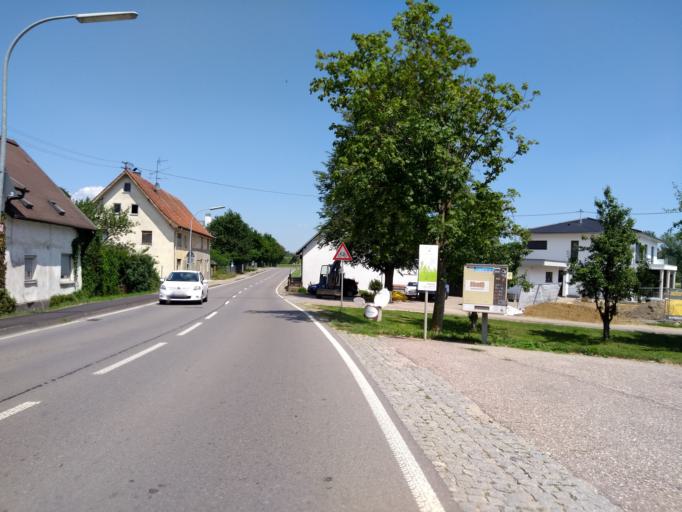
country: DE
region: Baden-Wuerttemberg
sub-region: Tuebingen Region
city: Dettingen
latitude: 48.2642
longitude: 9.7253
